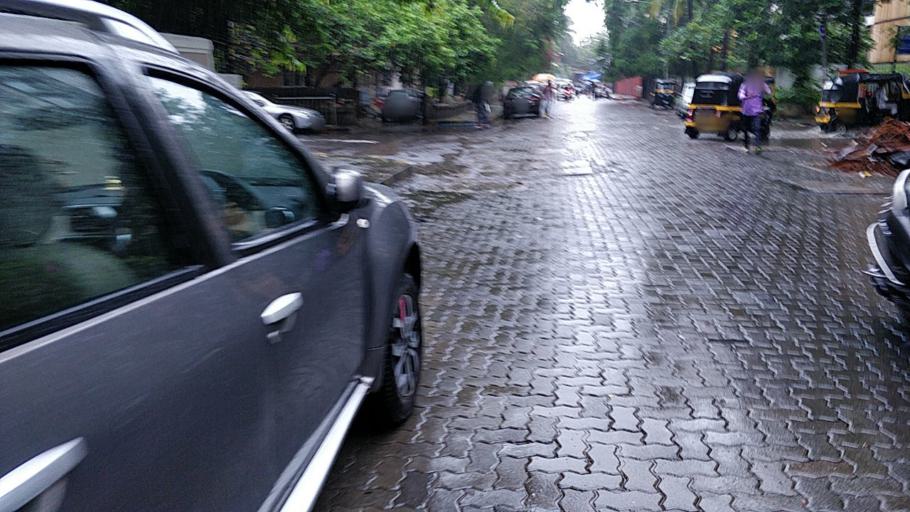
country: IN
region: Maharashtra
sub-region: Mumbai Suburban
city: Mumbai
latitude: 19.0770
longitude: 72.8330
